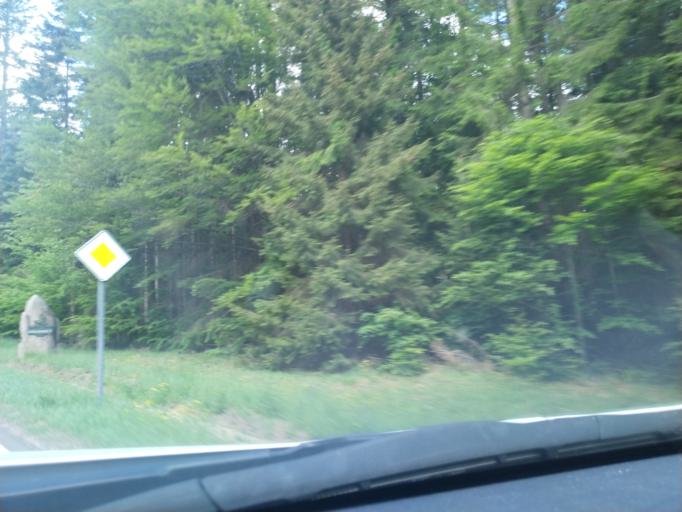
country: DE
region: Baden-Wuerttemberg
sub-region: Karlsruhe Region
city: Enzklosterle
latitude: 48.6117
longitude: 8.4539
